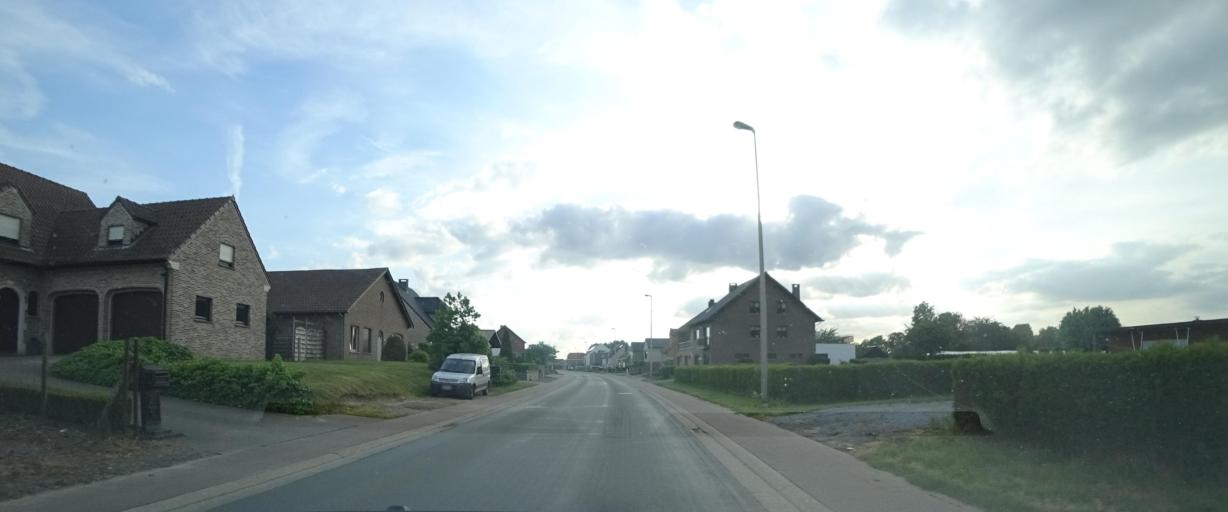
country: BE
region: Flanders
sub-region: Provincie Limburg
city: Nieuwerkerken
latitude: 50.8635
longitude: 5.1755
